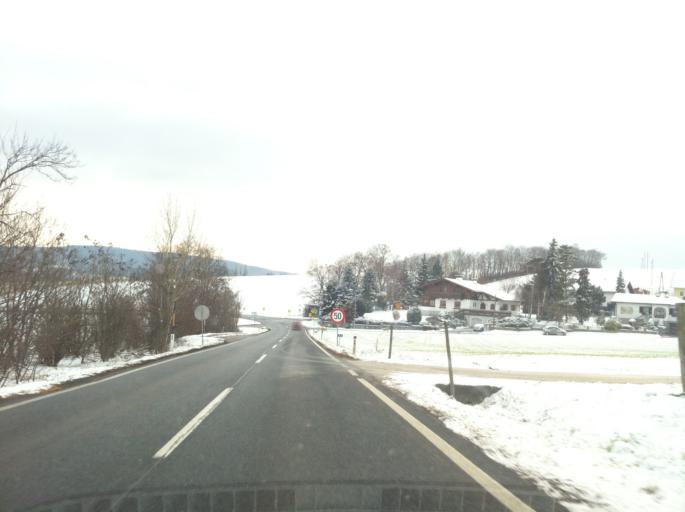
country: AT
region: Lower Austria
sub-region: Politischer Bezirk Tulln
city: Tulln
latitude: 48.2768
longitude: 16.0712
